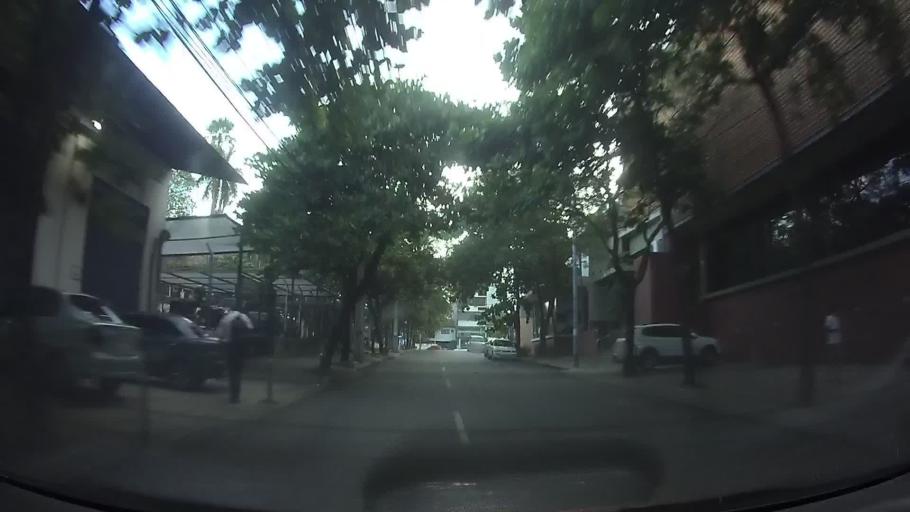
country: PY
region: Asuncion
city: Asuncion
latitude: -25.2852
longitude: -57.5736
